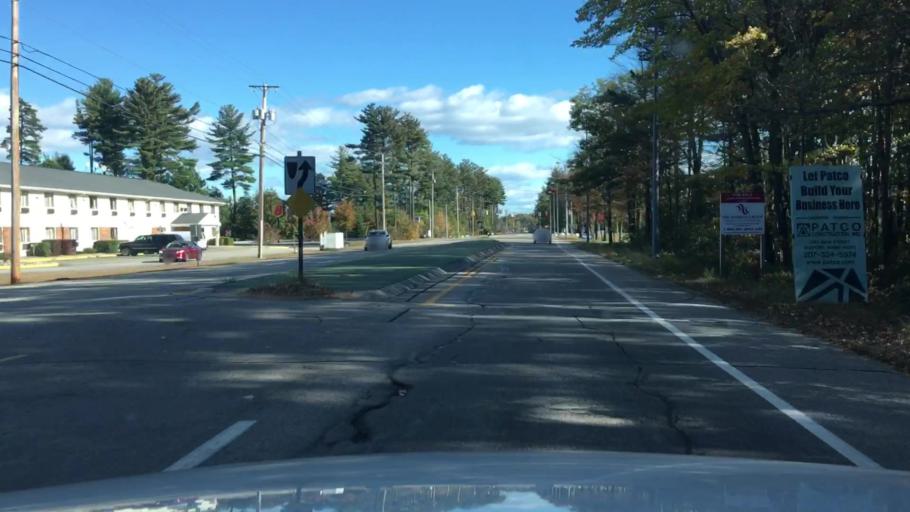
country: US
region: Maine
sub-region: York County
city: South Sanford
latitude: 43.4006
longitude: -70.7052
